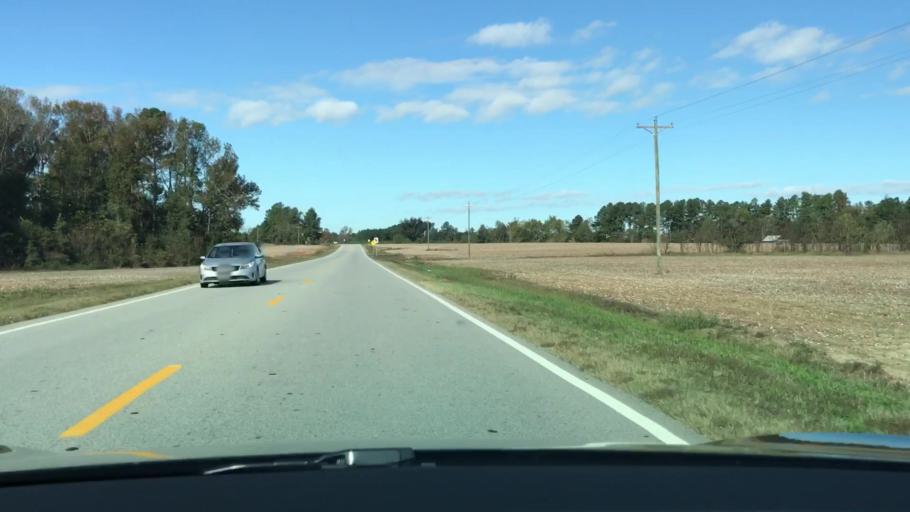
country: US
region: Georgia
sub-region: Jefferson County
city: Wrens
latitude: 33.2563
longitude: -82.4687
